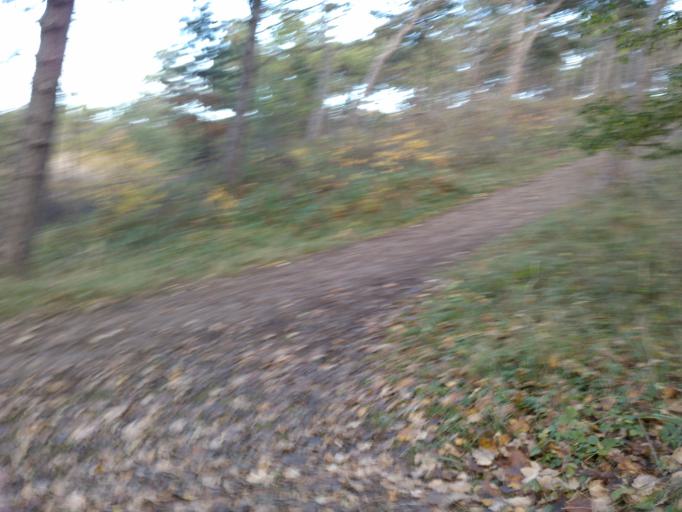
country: NL
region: South Holland
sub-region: Gemeente Noordwijkerhout
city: Noordwijkerhout
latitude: 52.2812
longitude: 4.4725
